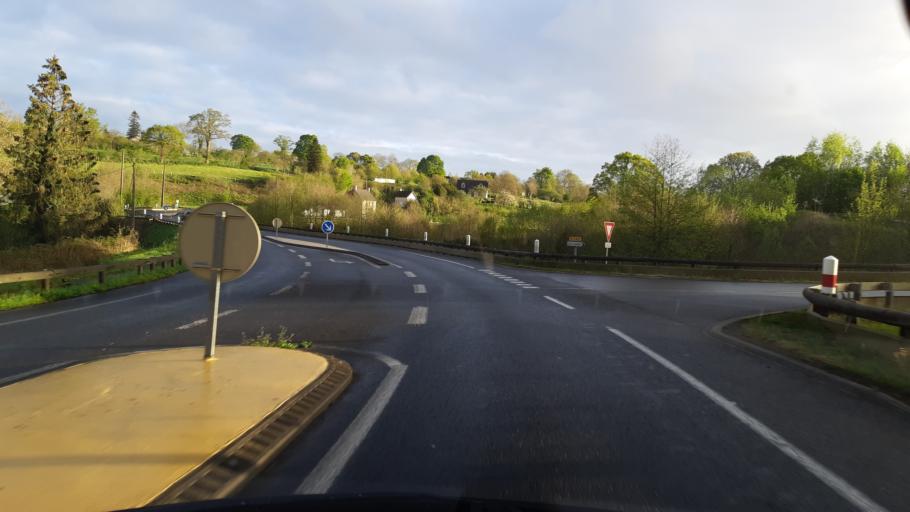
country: FR
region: Lower Normandy
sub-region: Departement de la Manche
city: Agneaux
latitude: 49.0694
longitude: -1.1298
